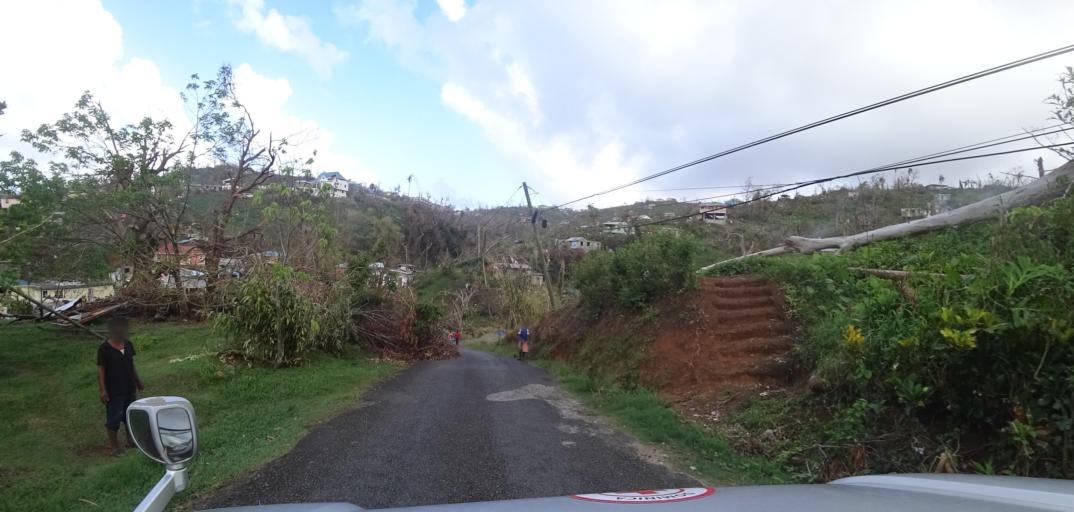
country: DM
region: Saint Andrew
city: Marigot
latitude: 15.5383
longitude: -61.2857
